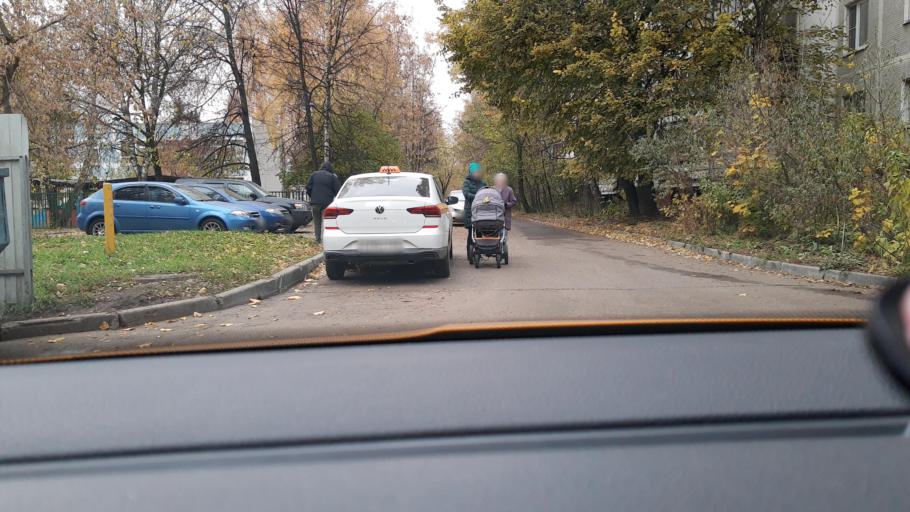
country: RU
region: Moscow
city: Kozeyevo
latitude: 55.8954
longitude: 37.6298
